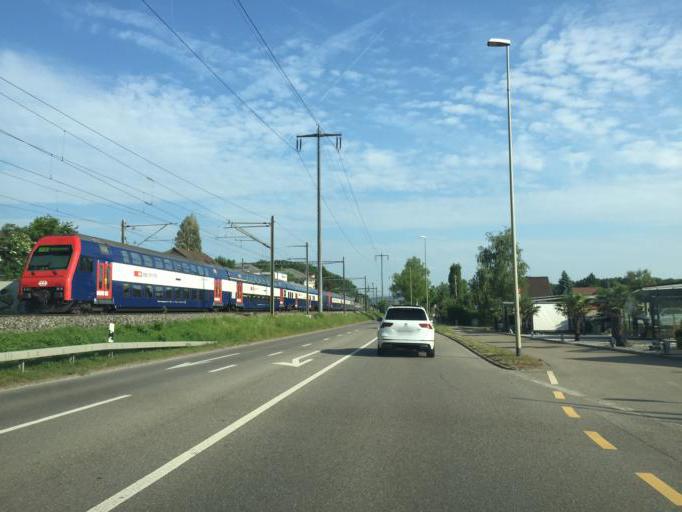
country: CH
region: Zurich
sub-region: Bezirk Dielsdorf
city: Oberglatt / Bahnhofquartier
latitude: 47.4668
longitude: 8.5134
